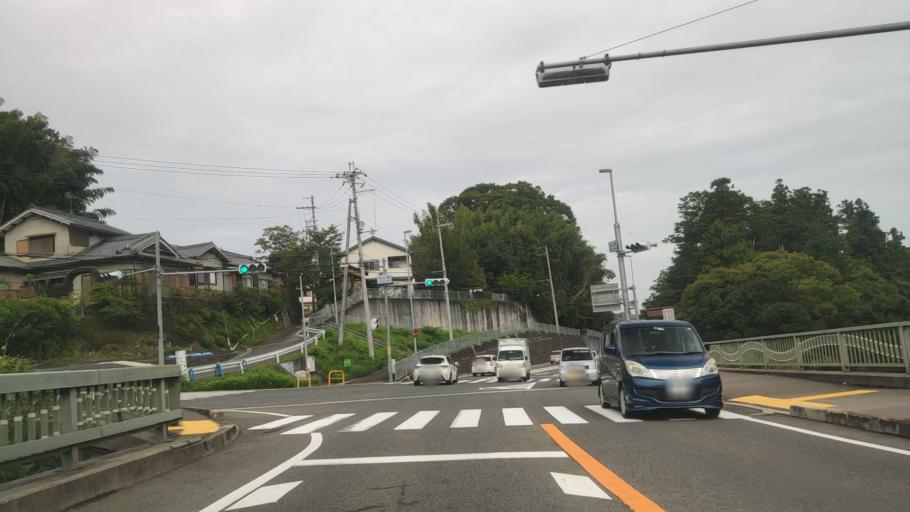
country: JP
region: Osaka
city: Tondabayashicho
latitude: 34.4220
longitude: 135.5784
